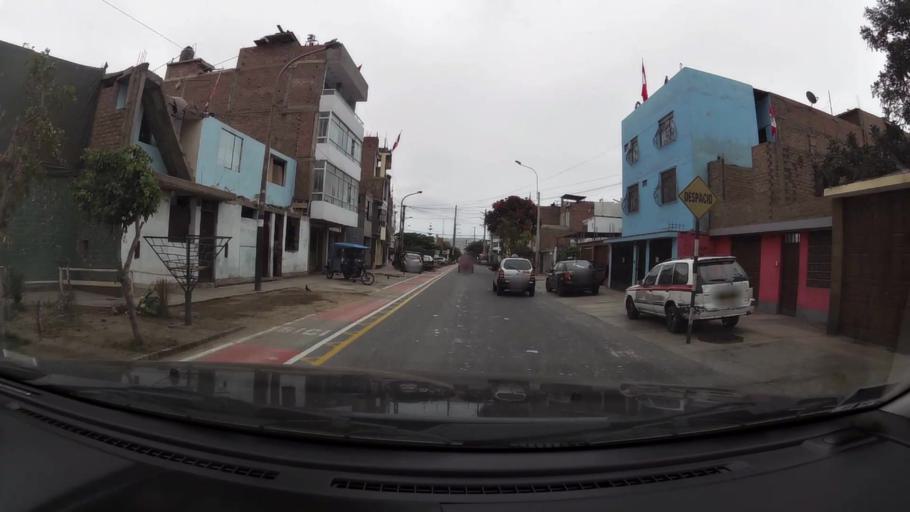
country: PE
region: Lima
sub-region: Lima
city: Surco
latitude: -12.1439
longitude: -77.0078
